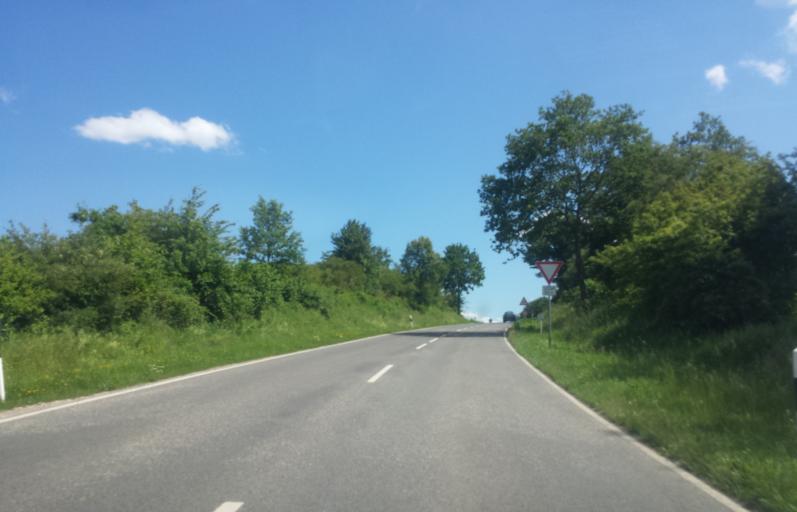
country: DE
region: Bavaria
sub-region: Upper Franconia
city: Hirschaid
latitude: 49.8036
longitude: 10.9739
